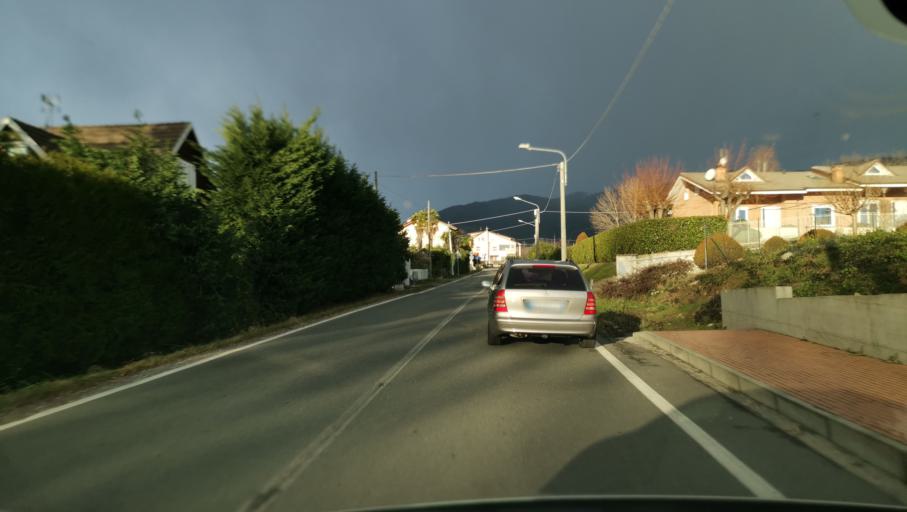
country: IT
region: Piedmont
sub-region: Provincia di Torino
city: Coazze
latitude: 45.0515
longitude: 7.3237
